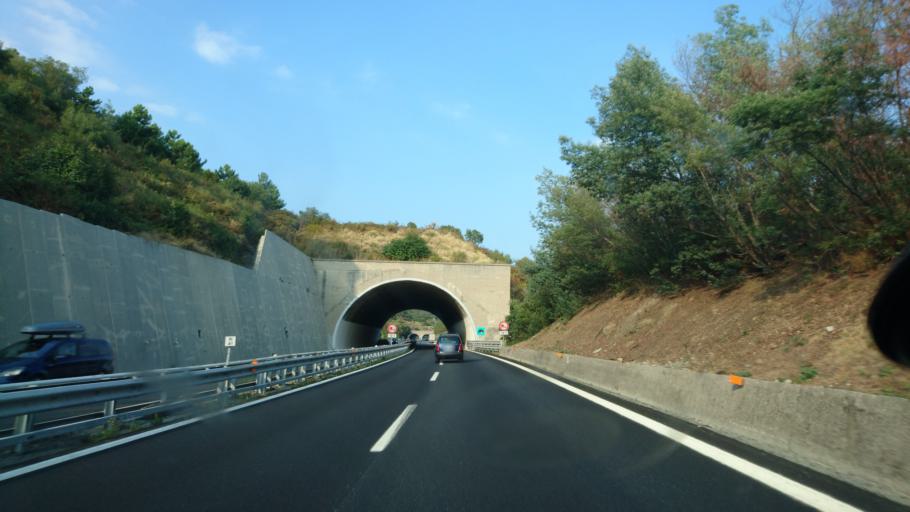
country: IT
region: Liguria
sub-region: Provincia di Savona
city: Savona
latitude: 44.3092
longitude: 8.4660
